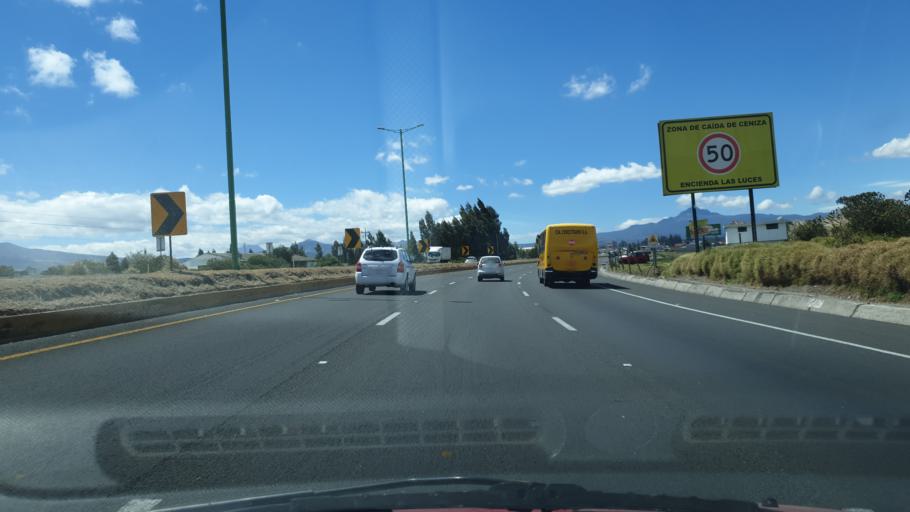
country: EC
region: Cotopaxi
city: Saquisili
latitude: -0.8128
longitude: -78.6252
